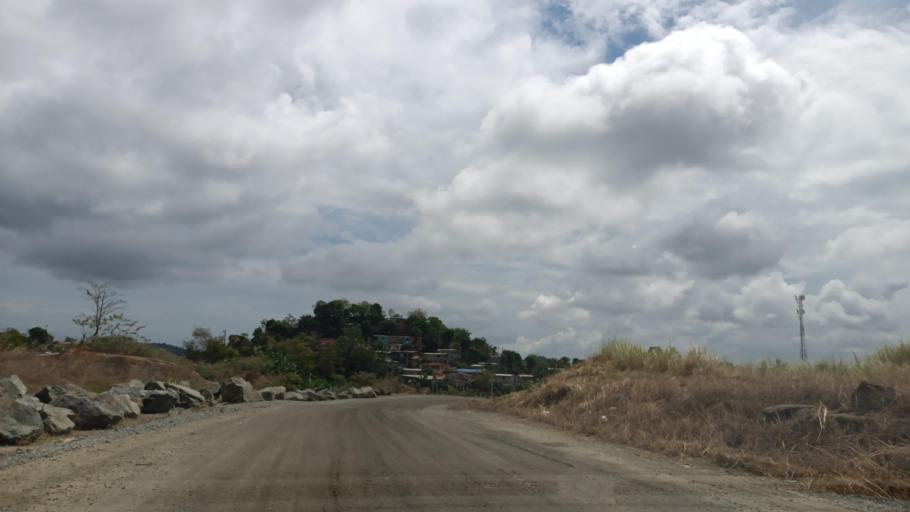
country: PA
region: Panama
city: Las Cumbres
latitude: 9.1038
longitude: -79.4987
